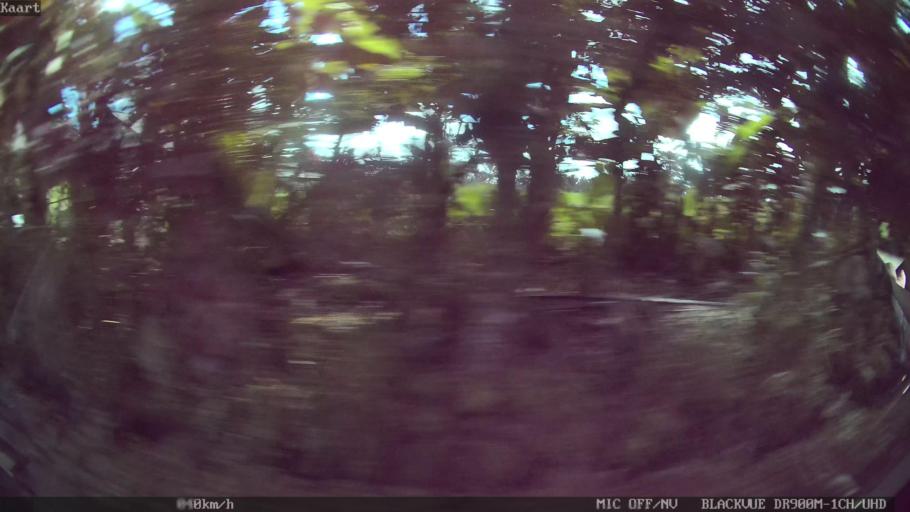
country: ID
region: Bali
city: Banjar Apuan Kaja
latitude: -8.4859
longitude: 115.3427
